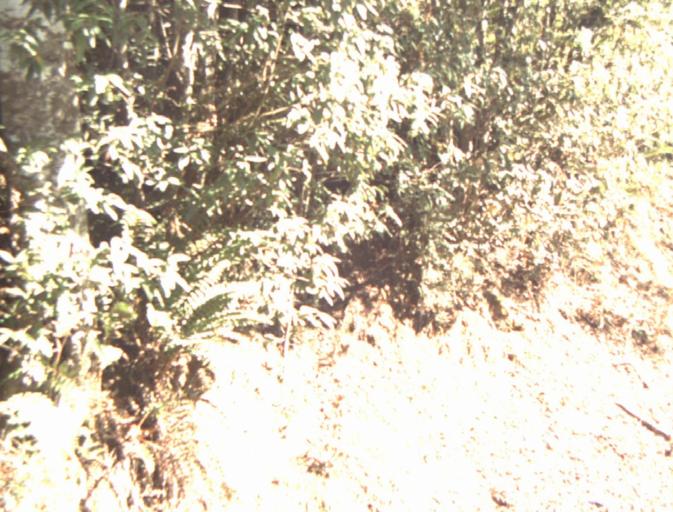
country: AU
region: Tasmania
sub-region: Dorset
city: Scottsdale
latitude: -41.2792
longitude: 147.3593
